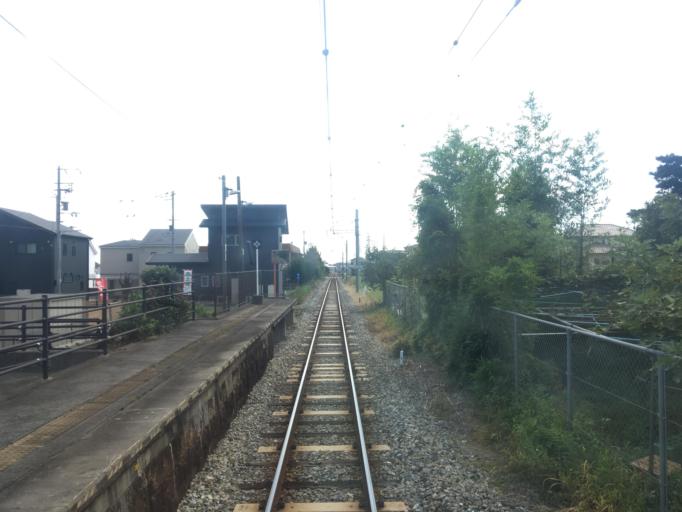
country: JP
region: Hyogo
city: Yashiro
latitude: 34.9491
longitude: 134.9626
